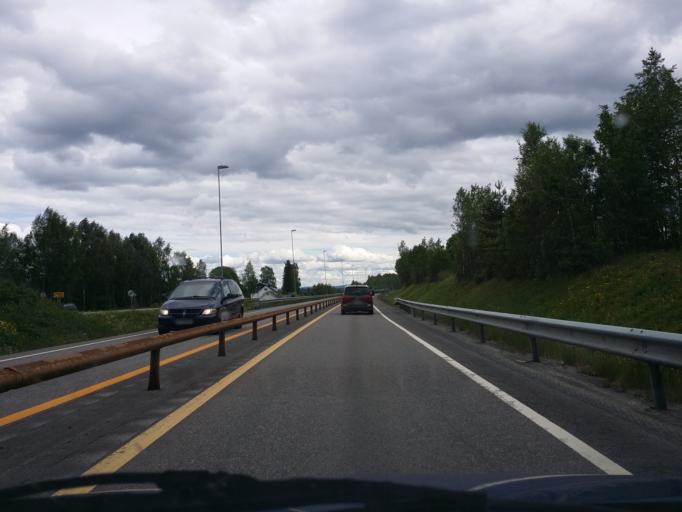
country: NO
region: Hedmark
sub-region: Hamar
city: Hamar
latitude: 60.8490
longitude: 11.0227
